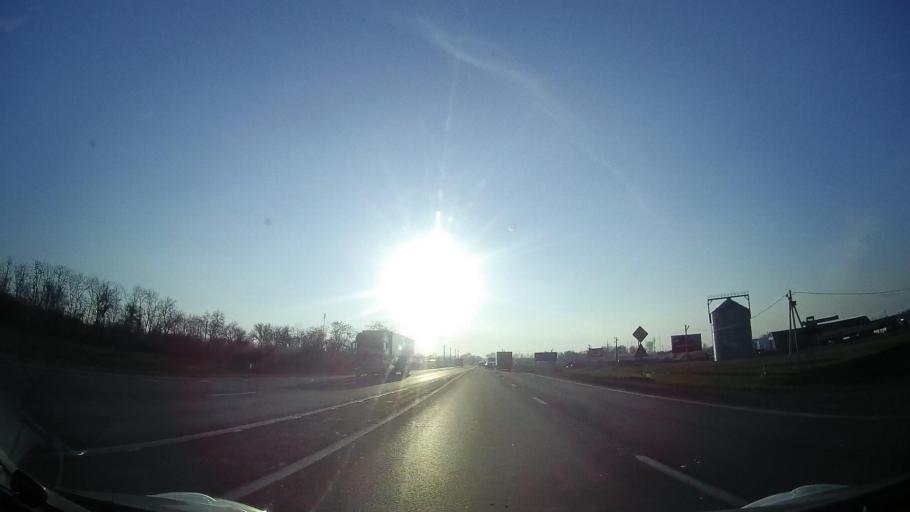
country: RU
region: Rostov
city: Bataysk
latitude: 47.0834
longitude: 39.7784
